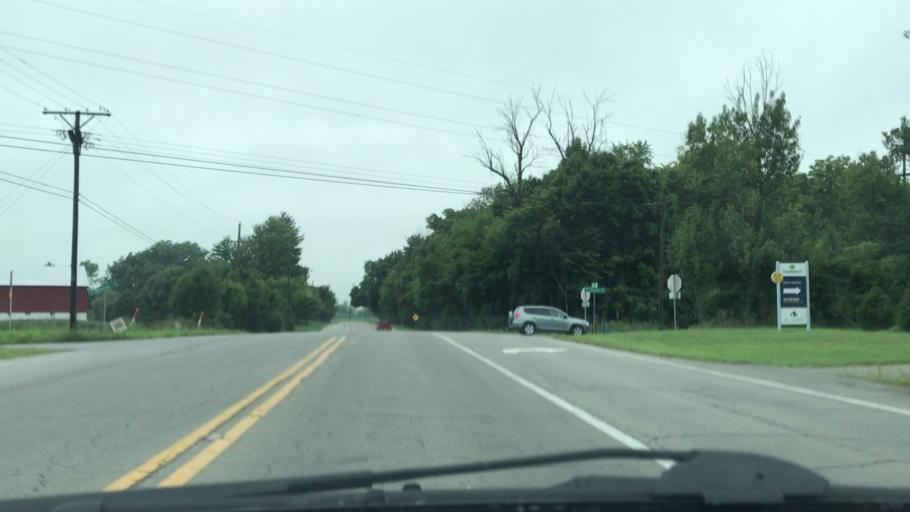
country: US
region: Indiana
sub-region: Hamilton County
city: Westfield
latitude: 40.0779
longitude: -86.0900
